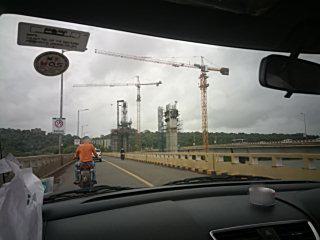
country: IN
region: Goa
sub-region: North Goa
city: Panaji
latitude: 15.5024
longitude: 73.8366
